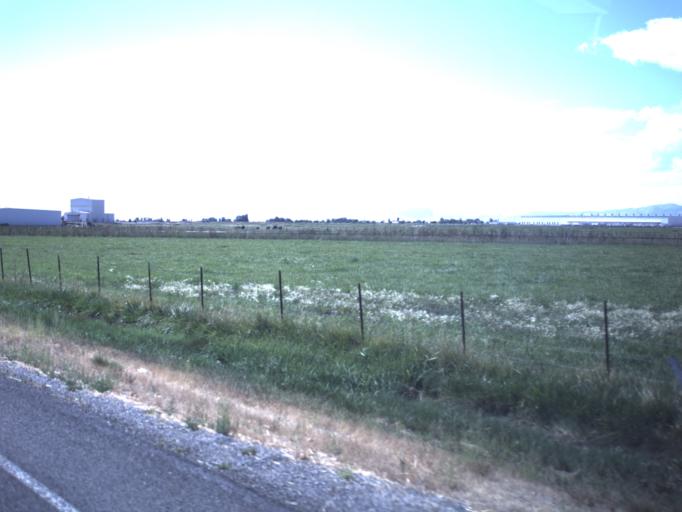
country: US
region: Utah
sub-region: Box Elder County
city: Honeyville
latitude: 41.5685
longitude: -112.1297
